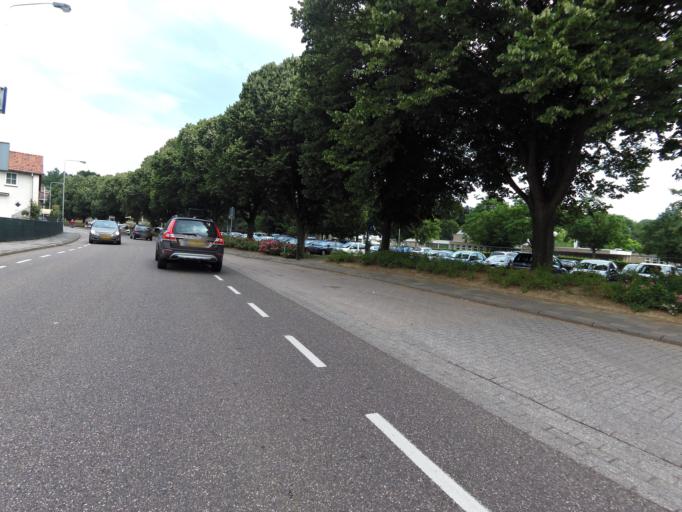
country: NL
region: Limburg
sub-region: Valkenburg aan de Geul
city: Valkenburg
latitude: 50.8636
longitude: 5.8372
